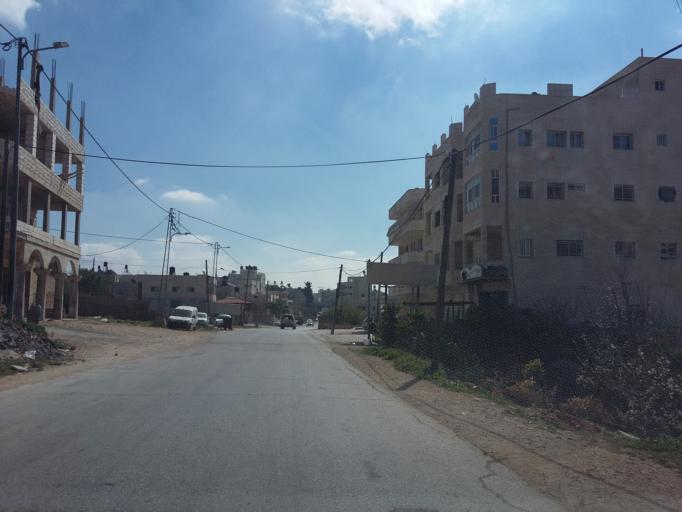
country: PS
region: West Bank
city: Al Jib
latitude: 31.8539
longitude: 35.1811
